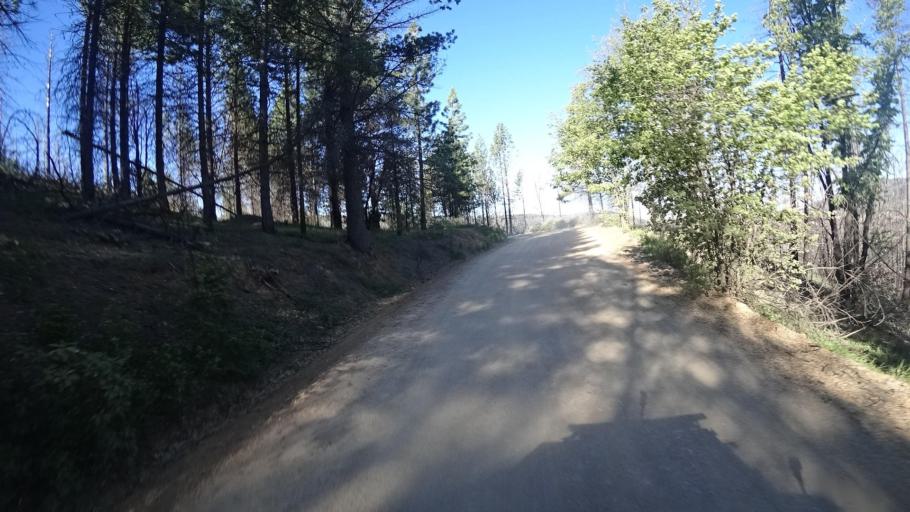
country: US
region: California
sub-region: Lake County
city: Upper Lake
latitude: 39.3351
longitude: -122.9572
